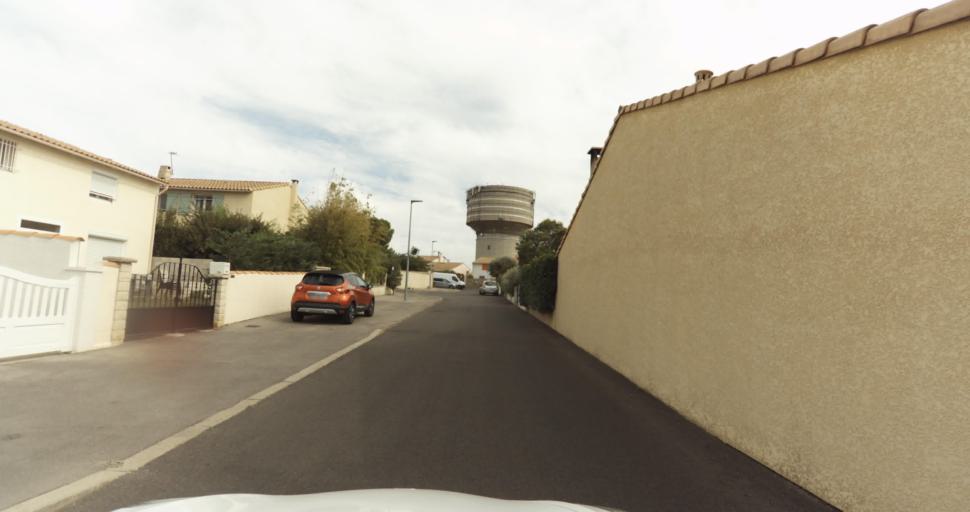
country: FR
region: Provence-Alpes-Cote d'Azur
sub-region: Departement des Bouches-du-Rhone
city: Miramas
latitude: 43.5739
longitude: 5.0042
